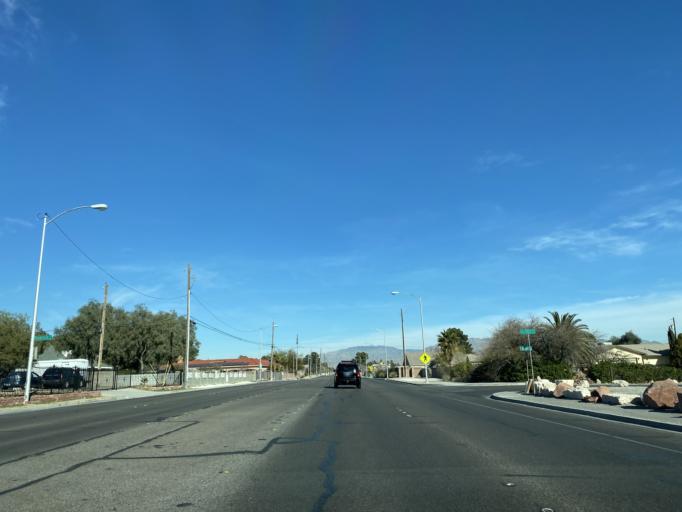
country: US
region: Nevada
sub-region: Clark County
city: Las Vegas
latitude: 36.2066
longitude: -115.2242
